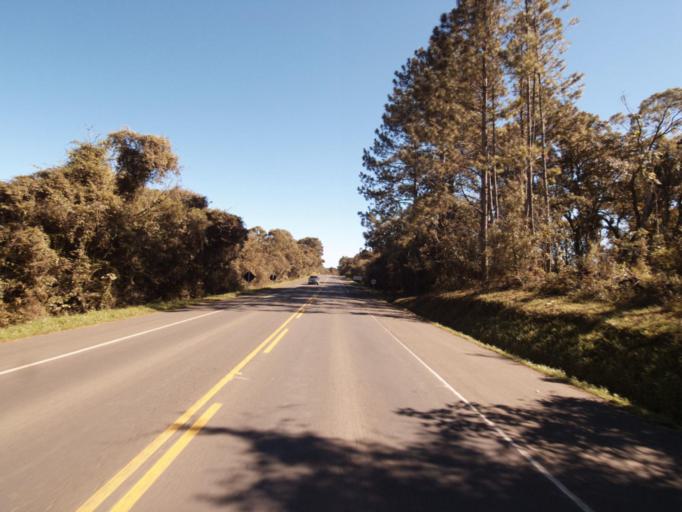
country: BR
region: Santa Catarina
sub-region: Joacaba
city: Joacaba
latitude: -27.1090
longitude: -51.6355
